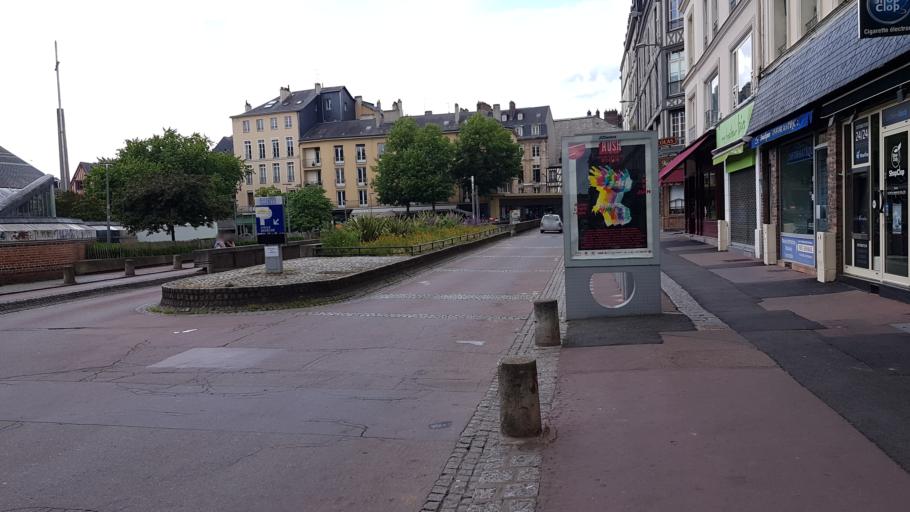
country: FR
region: Haute-Normandie
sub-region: Departement de la Seine-Maritime
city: Rouen
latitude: 49.4433
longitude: 1.0889
